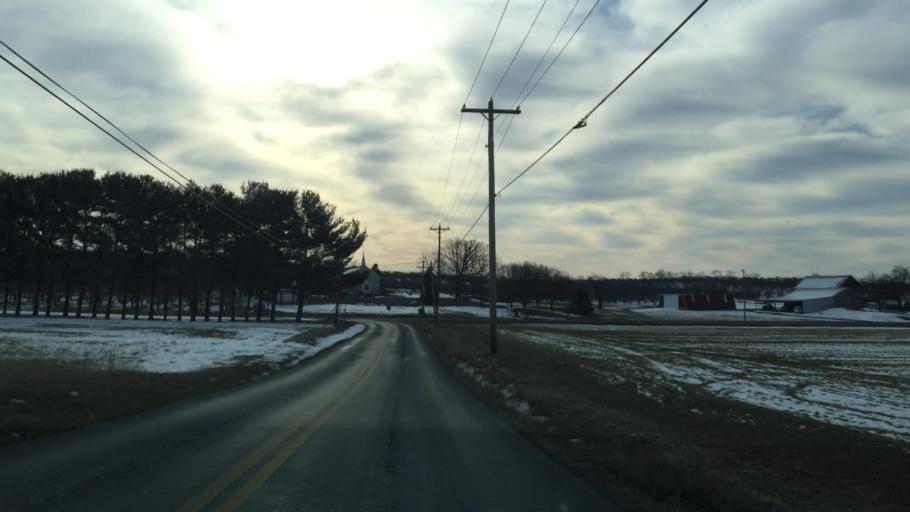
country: US
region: Virginia
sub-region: City of Winchester
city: Winchester
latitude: 39.2540
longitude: -78.1358
